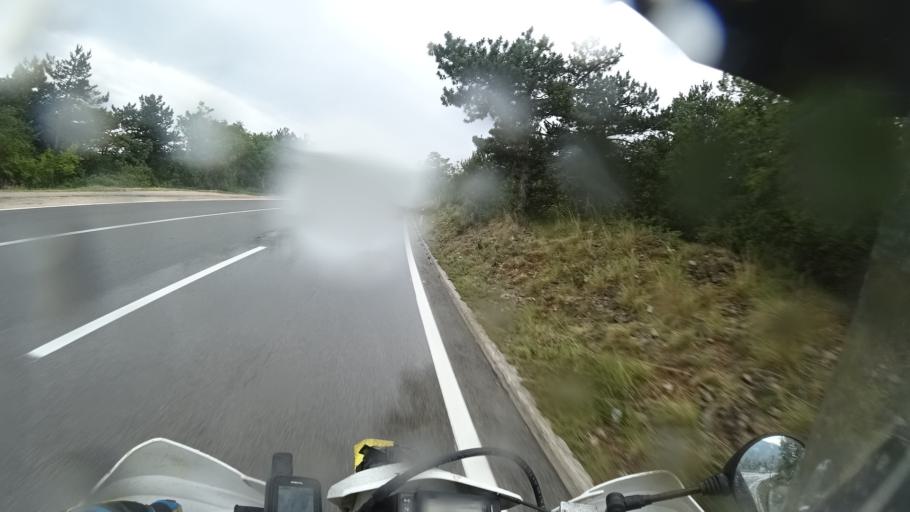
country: HR
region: Sibensko-Kniniska
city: Knin
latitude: 44.0417
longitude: 16.1851
